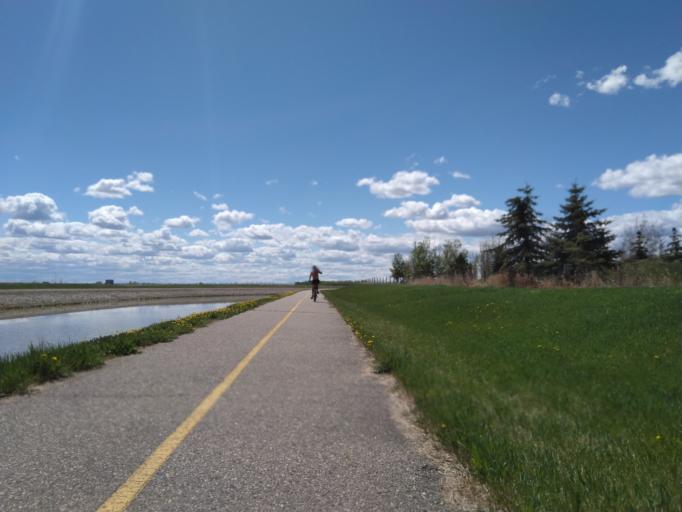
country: CA
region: Alberta
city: Chestermere
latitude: 51.0071
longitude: -113.8488
